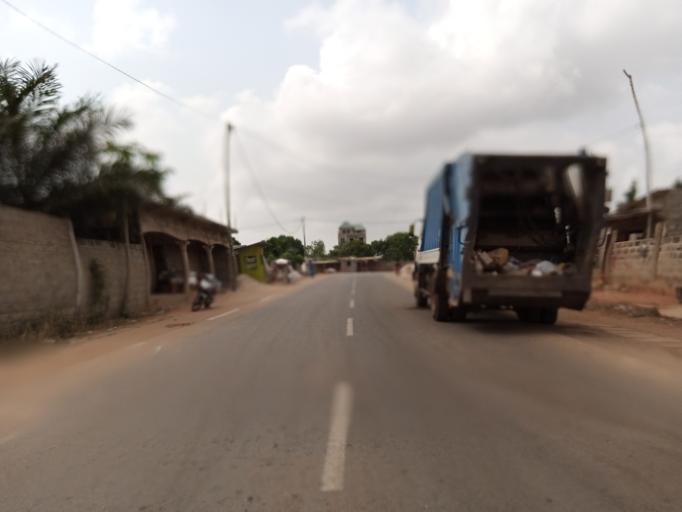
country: TG
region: Maritime
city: Lome
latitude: 6.2323
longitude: 1.0973
